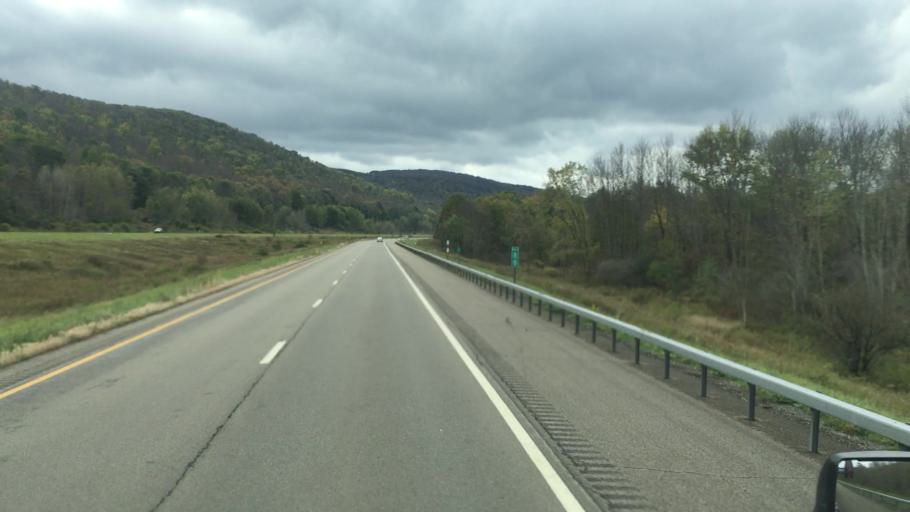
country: US
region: New York
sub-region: Allegany County
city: Cuba
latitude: 42.2000
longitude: -78.3314
